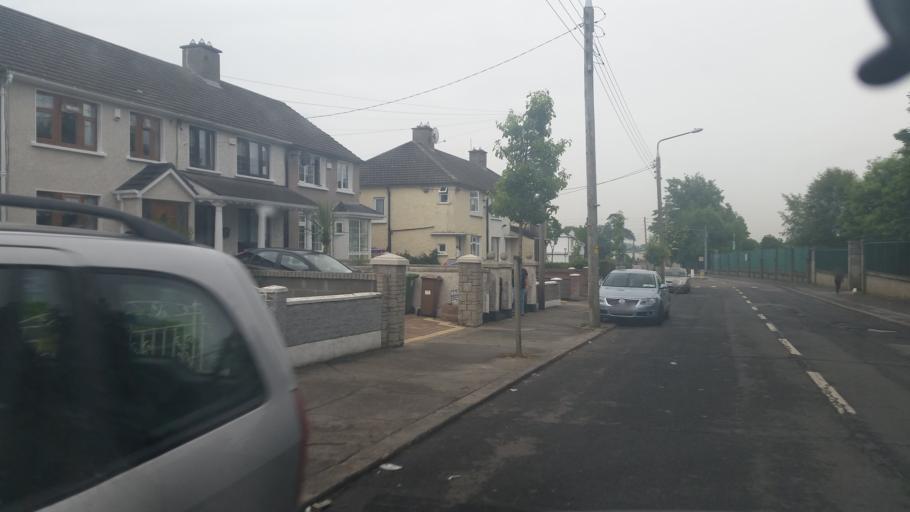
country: IE
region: Leinster
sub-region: Dublin City
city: Finglas
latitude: 53.3885
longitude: -6.3088
